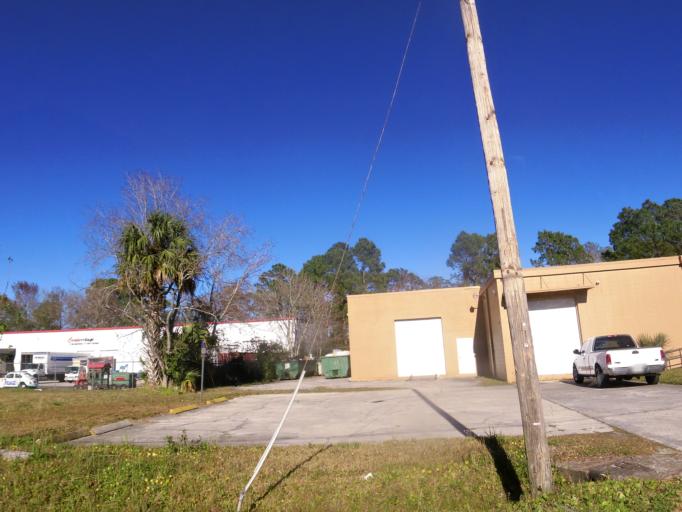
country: US
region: Florida
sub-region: Duval County
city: Jacksonville
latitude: 30.2718
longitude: -81.6263
